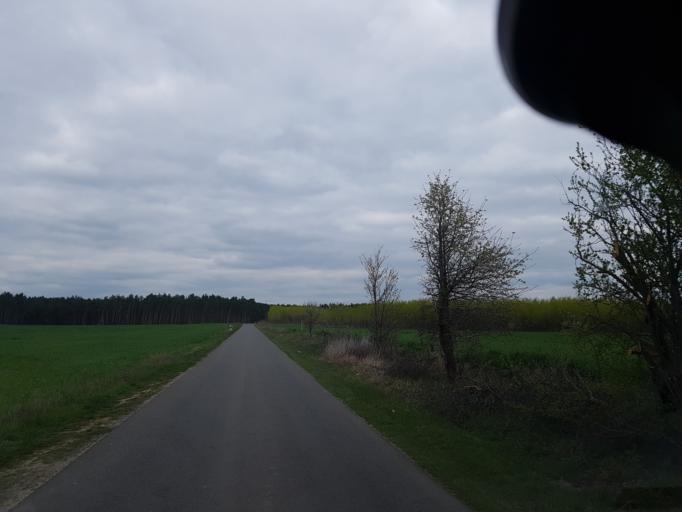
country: DE
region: Brandenburg
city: Linthe
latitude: 52.1206
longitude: 12.8017
